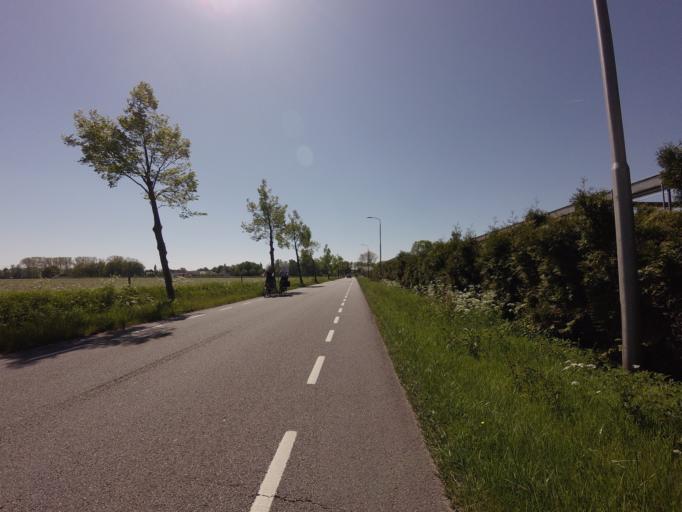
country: BE
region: Flanders
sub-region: Provincie Antwerpen
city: Essen
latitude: 51.4751
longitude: 4.4603
